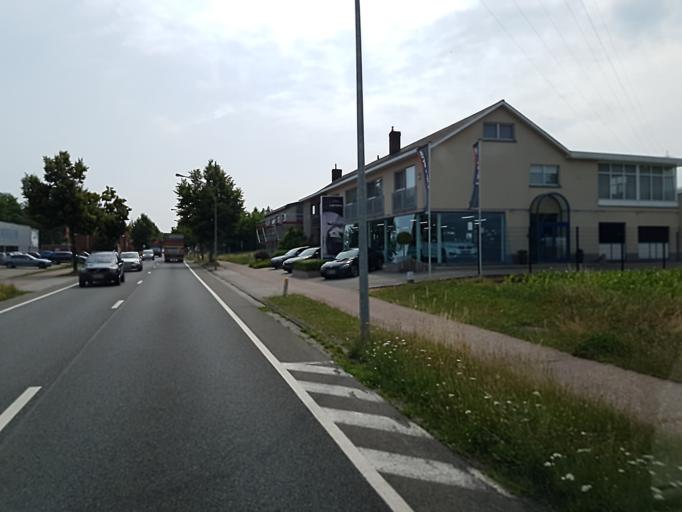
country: BE
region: Flanders
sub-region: Provincie Antwerpen
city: Balen
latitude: 51.1737
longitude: 5.1436
